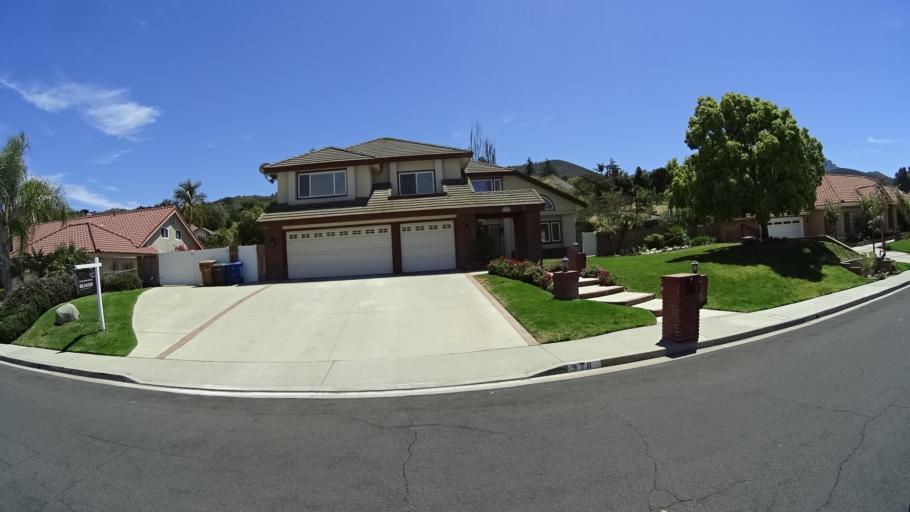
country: US
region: California
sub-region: Ventura County
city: Casa Conejo
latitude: 34.1597
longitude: -118.9450
